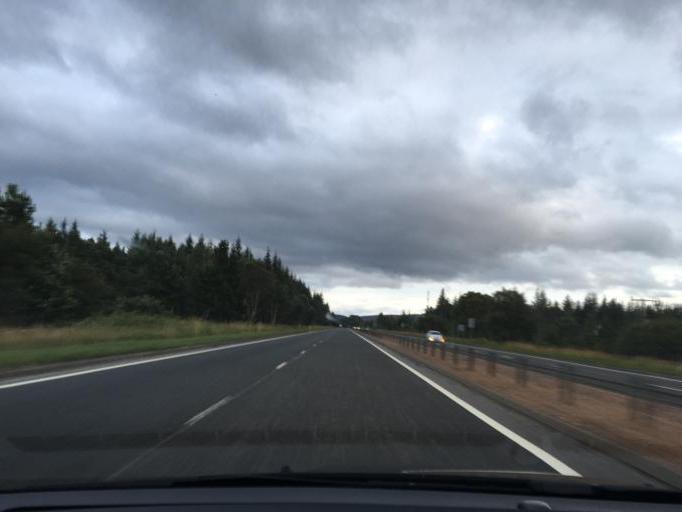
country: GB
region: Scotland
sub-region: Highland
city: Inverness
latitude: 57.4431
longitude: -4.1476
